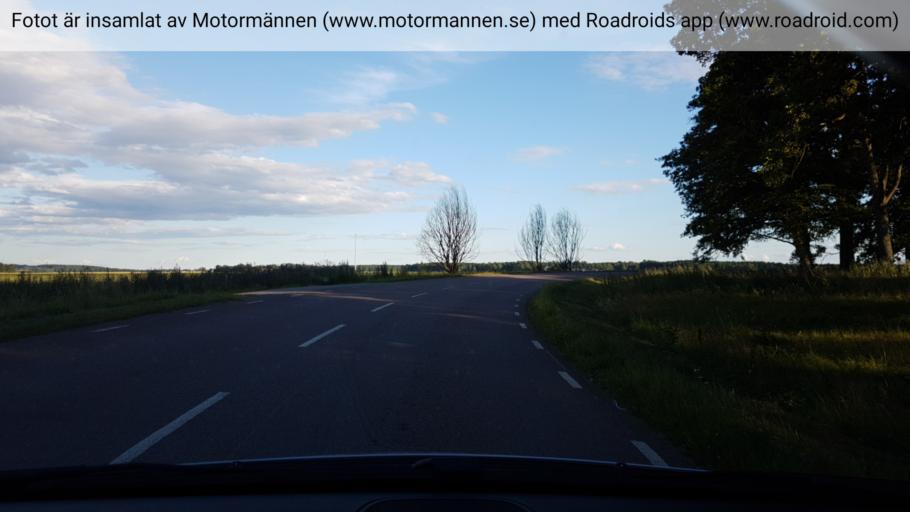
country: SE
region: Vaestmanland
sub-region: Vasteras
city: Tillberga
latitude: 59.7113
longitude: 16.6617
